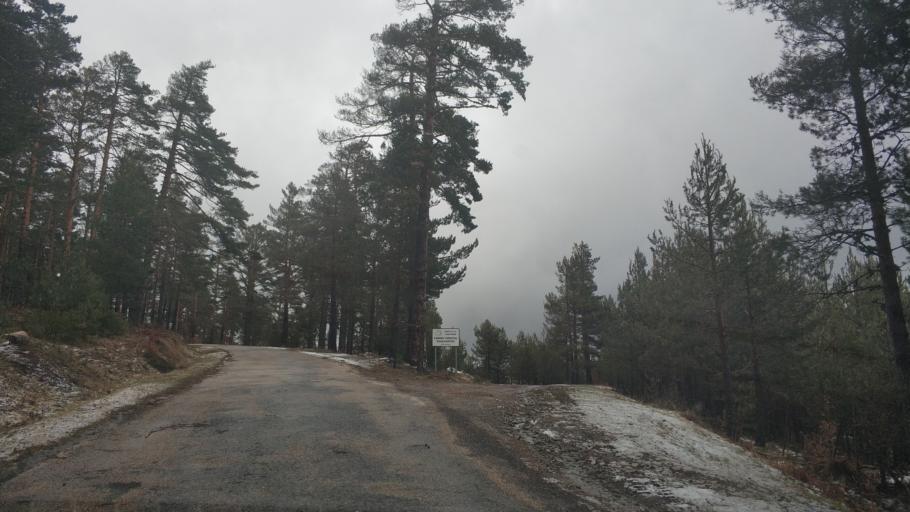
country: ES
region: Castille and Leon
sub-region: Provincia de Burgos
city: Neila
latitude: 42.0467
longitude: -3.0236
